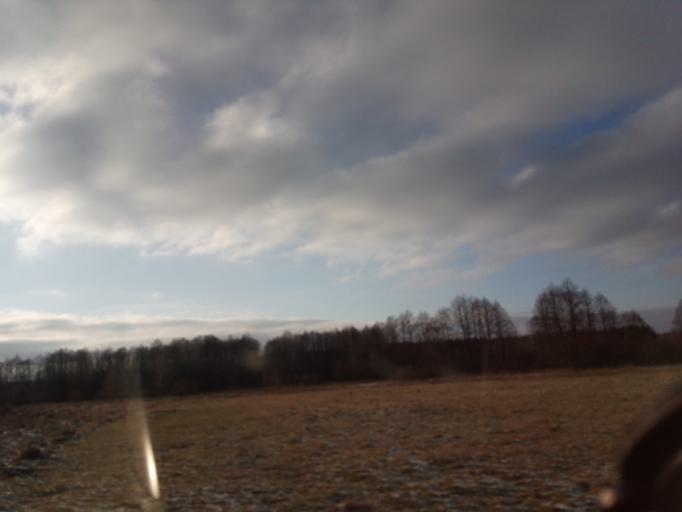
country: LT
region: Alytaus apskritis
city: Druskininkai
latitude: 53.9765
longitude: 24.2403
